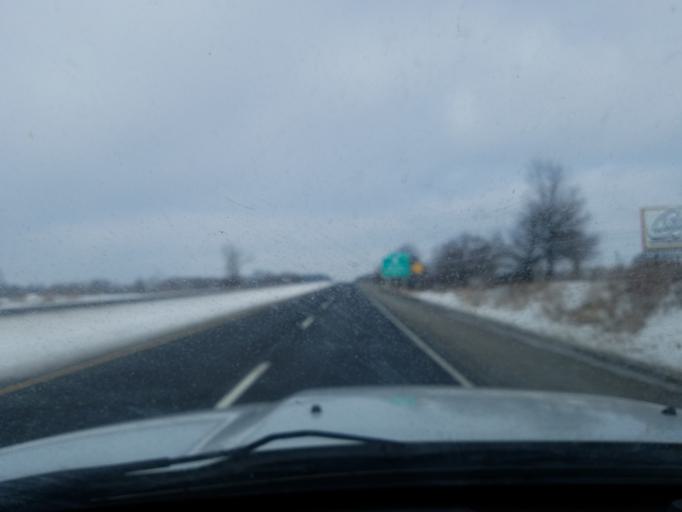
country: US
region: Indiana
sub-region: Marshall County
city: Plymouth
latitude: 41.3294
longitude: -86.2758
